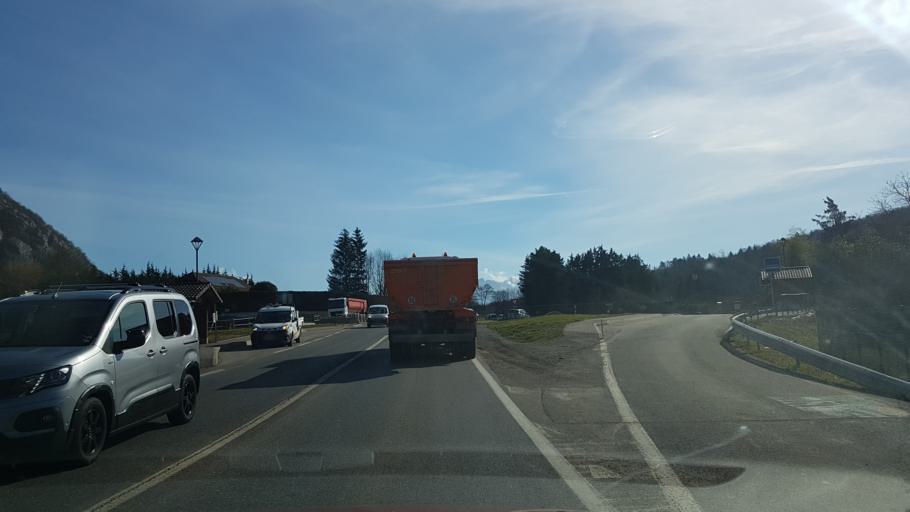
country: FR
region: Rhone-Alpes
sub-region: Departement de la Haute-Savoie
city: Sillingy
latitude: 45.9450
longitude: 6.0523
